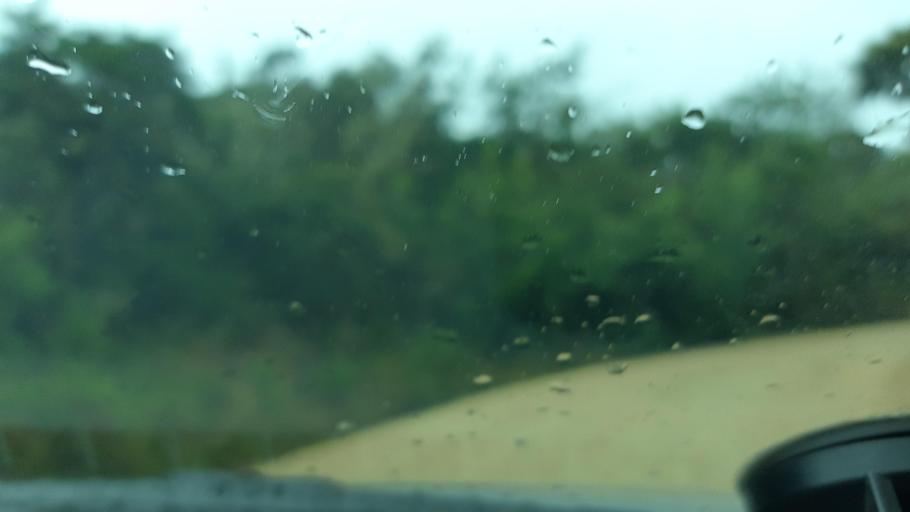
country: CO
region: Cundinamarca
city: Villapinzon
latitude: 5.2075
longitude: -73.5594
